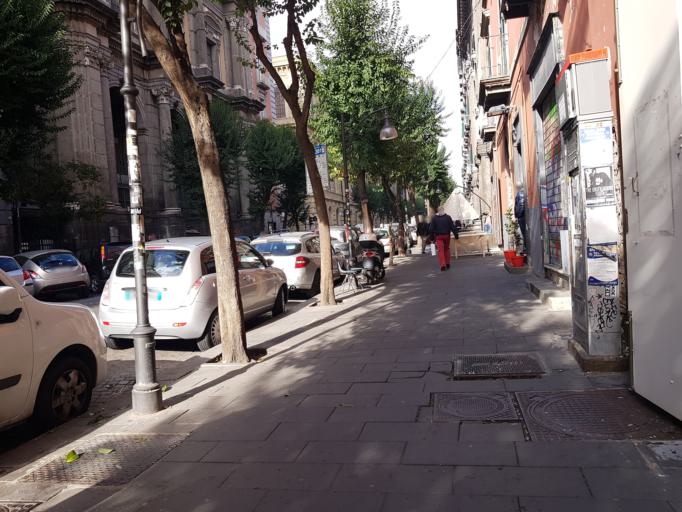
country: IT
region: Campania
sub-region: Provincia di Napoli
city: Napoli
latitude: 40.8507
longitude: 14.2520
